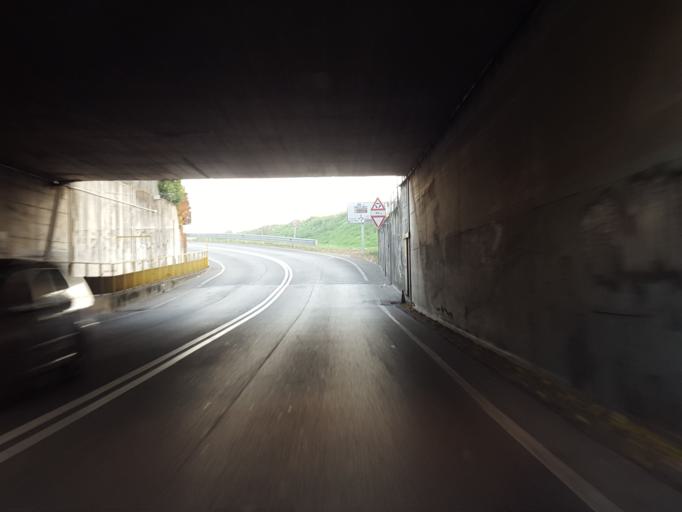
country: IT
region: Veneto
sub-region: Provincia di Vicenza
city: Vicenza
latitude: 45.5418
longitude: 11.5577
